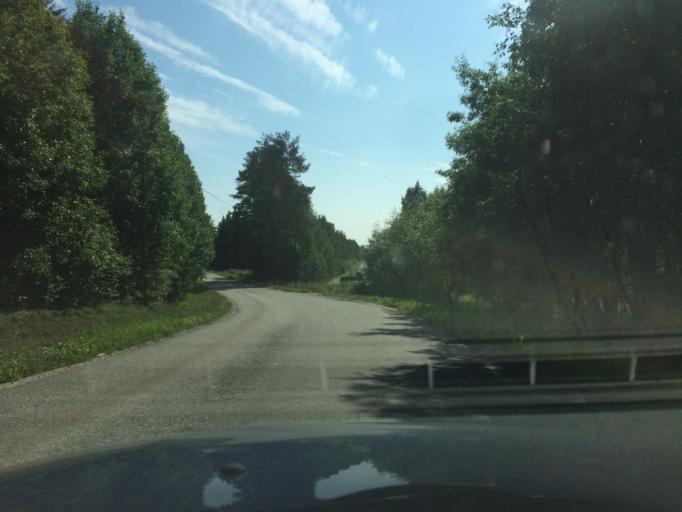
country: SE
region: Norrbotten
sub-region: Pitea Kommun
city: Norrfjarden
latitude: 65.3731
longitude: 21.3915
